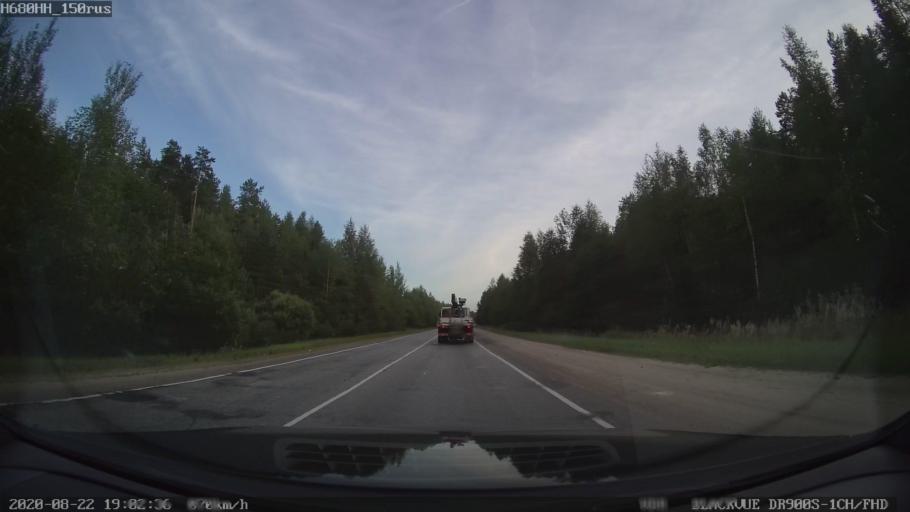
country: RU
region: Tverskaya
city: Sakharovo
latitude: 57.1071
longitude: 36.1204
